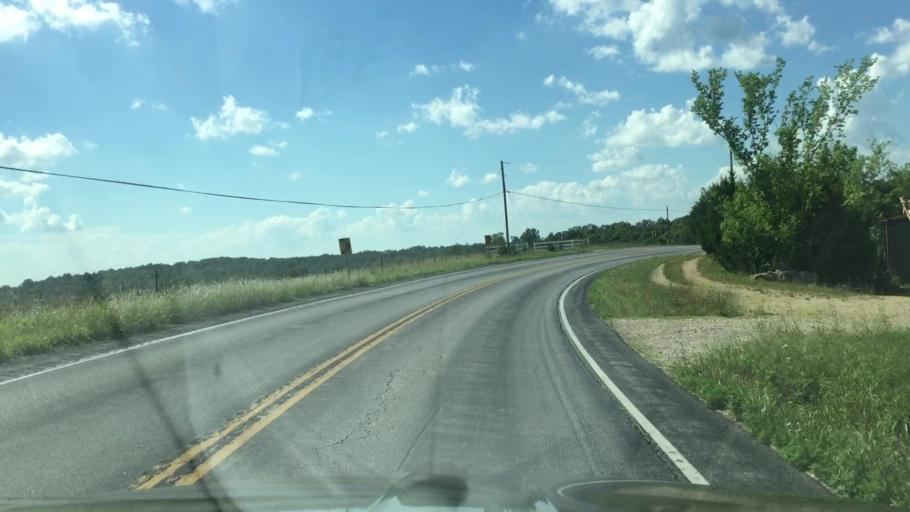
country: US
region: Missouri
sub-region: Miller County
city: Tuscumbia
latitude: 38.1005
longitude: -92.4979
